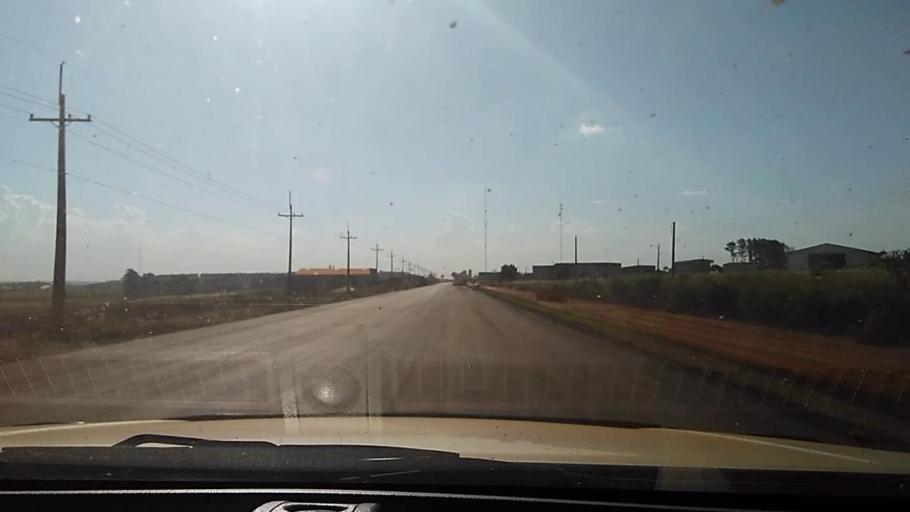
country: PY
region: Alto Parana
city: Naranjal
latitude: -25.9028
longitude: -55.4517
